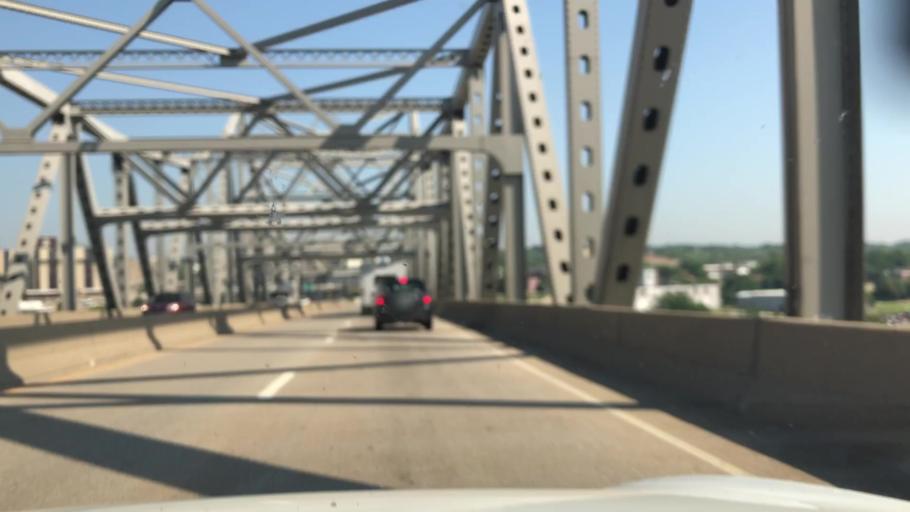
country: US
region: Illinois
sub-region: Peoria County
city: Peoria
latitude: 40.6899
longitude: -89.5843
